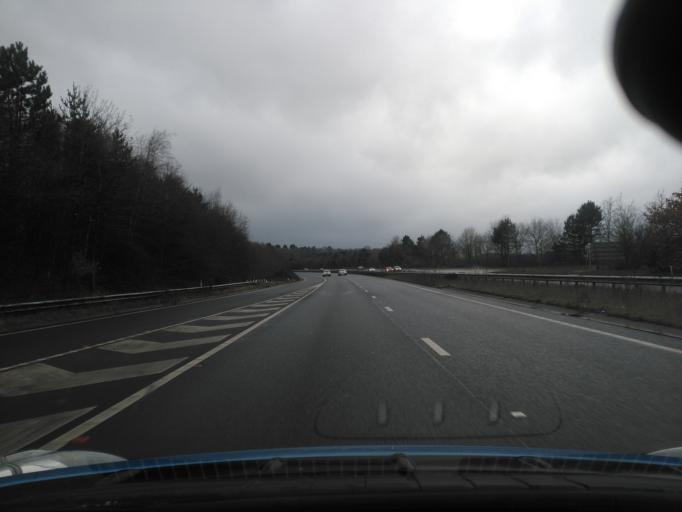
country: GB
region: England
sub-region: Surrey
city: Milford
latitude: 51.1776
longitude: -0.6541
